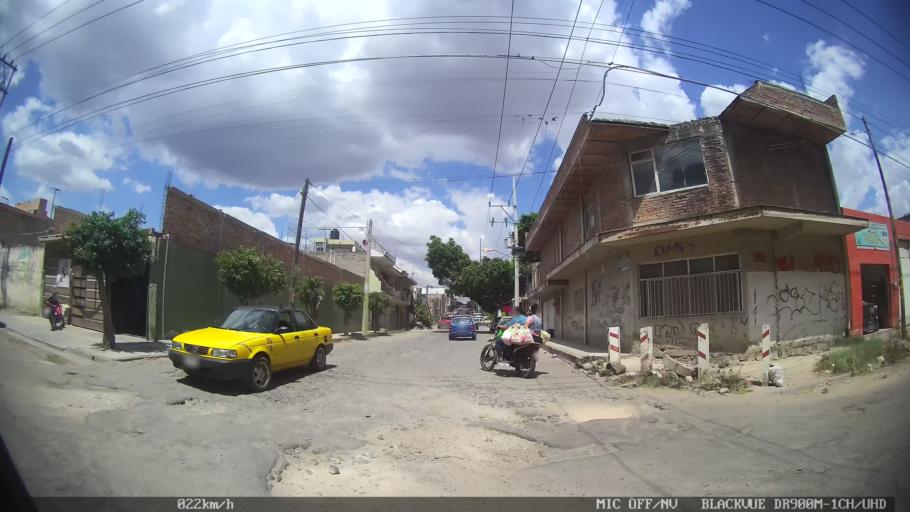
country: MX
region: Jalisco
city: Tlaquepaque
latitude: 20.6698
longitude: -103.2641
